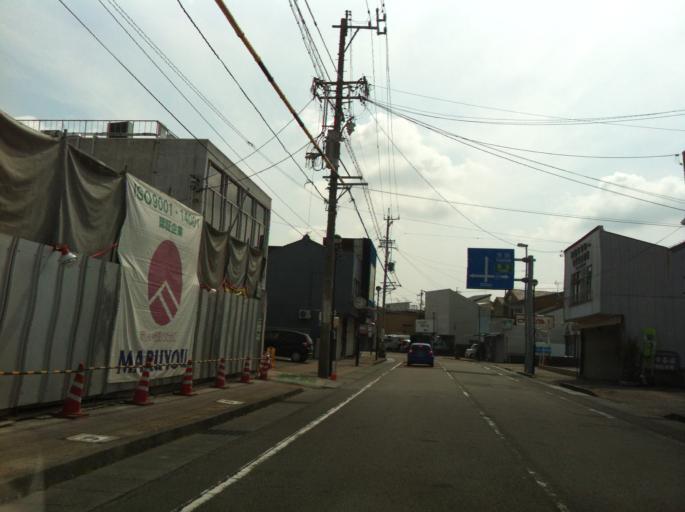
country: JP
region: Shizuoka
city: Shimada
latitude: 34.8322
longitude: 138.1807
